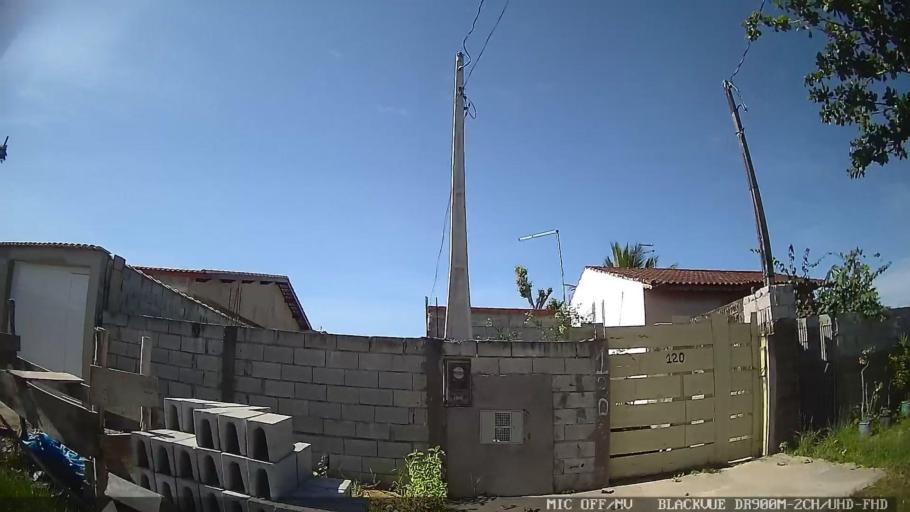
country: BR
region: Sao Paulo
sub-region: Itanhaem
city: Itanhaem
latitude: -24.2123
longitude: -46.8597
